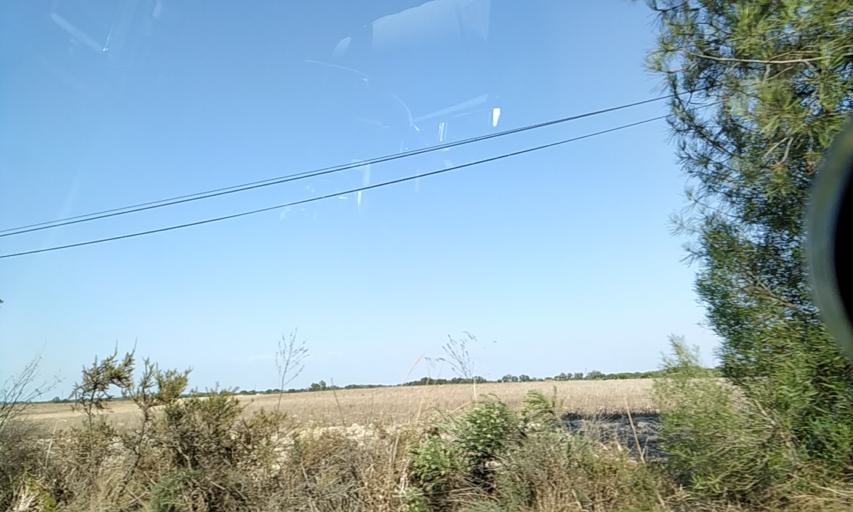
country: PT
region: Santarem
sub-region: Benavente
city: Poceirao
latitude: 38.7500
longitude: -8.6317
